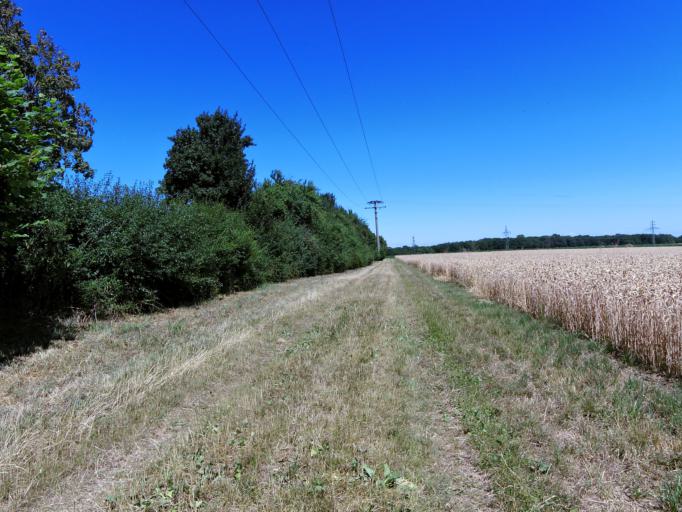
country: DE
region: Bavaria
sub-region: Regierungsbezirk Unterfranken
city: Theilheim
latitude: 49.7742
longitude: 10.0306
